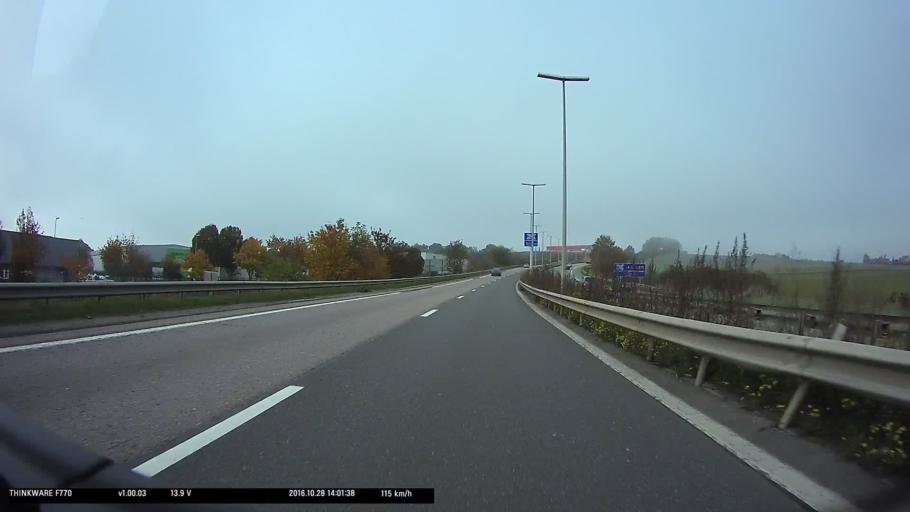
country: FR
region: Lorraine
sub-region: Departement de Meurthe-et-Moselle
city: Fleville-devant-Nancy
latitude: 48.6188
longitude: 6.1950
